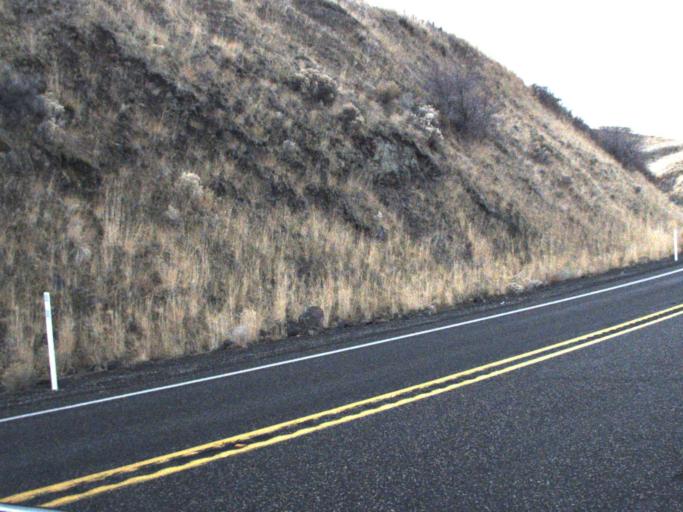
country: US
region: Washington
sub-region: Garfield County
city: Pomeroy
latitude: 46.4441
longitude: -117.4032
